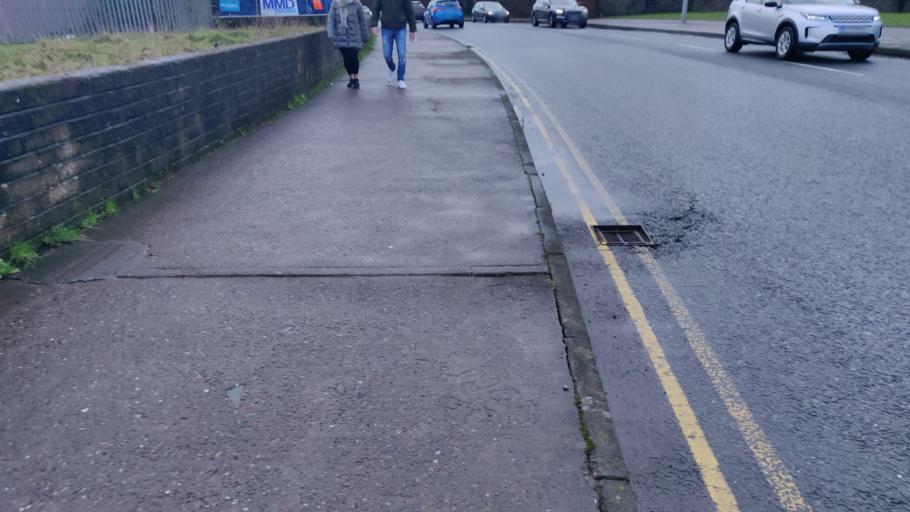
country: IE
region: Munster
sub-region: County Cork
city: Cork
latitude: 51.8788
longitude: -8.4345
